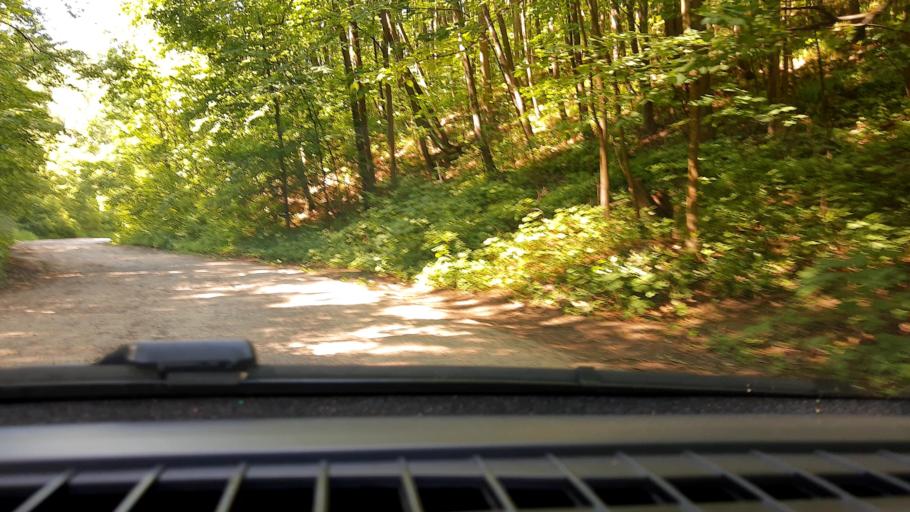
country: RU
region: Nizjnij Novgorod
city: Nizhniy Novgorod
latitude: 56.2266
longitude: 43.9291
